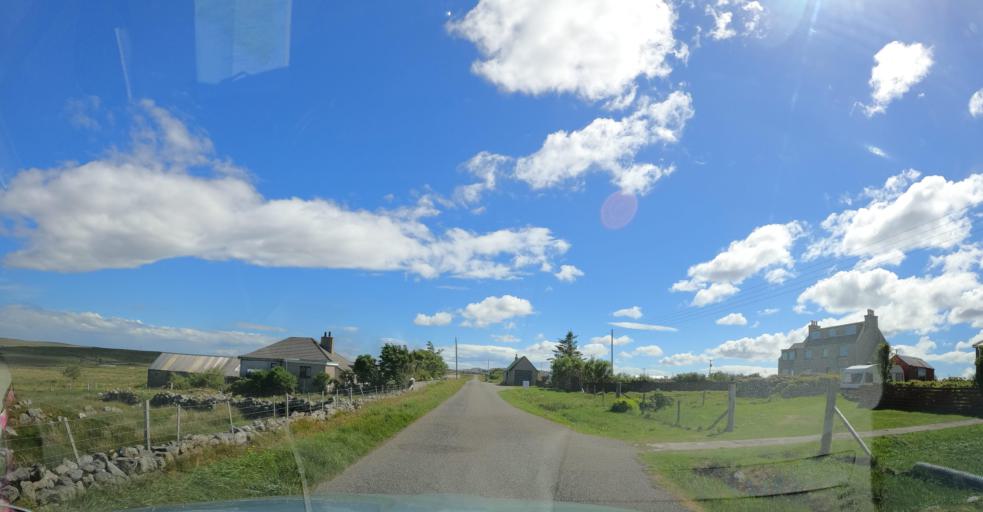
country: GB
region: Scotland
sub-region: Eilean Siar
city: Isle of Lewis
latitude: 58.3514
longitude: -6.5465
